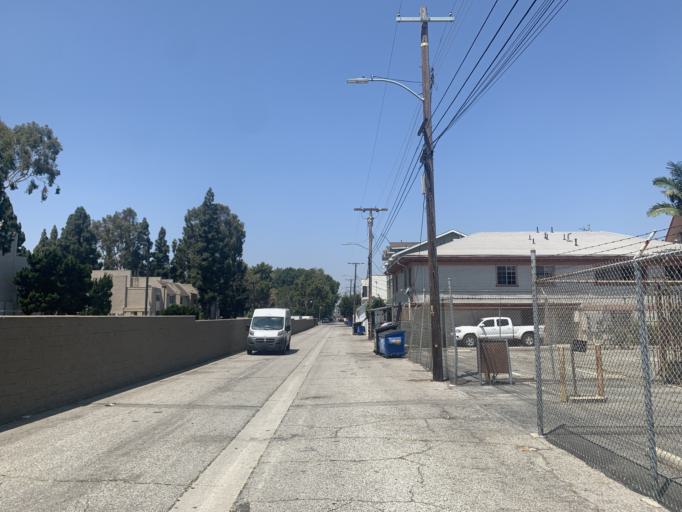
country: US
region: California
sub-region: Los Angeles County
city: Los Angeles
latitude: 34.0270
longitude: -118.2864
